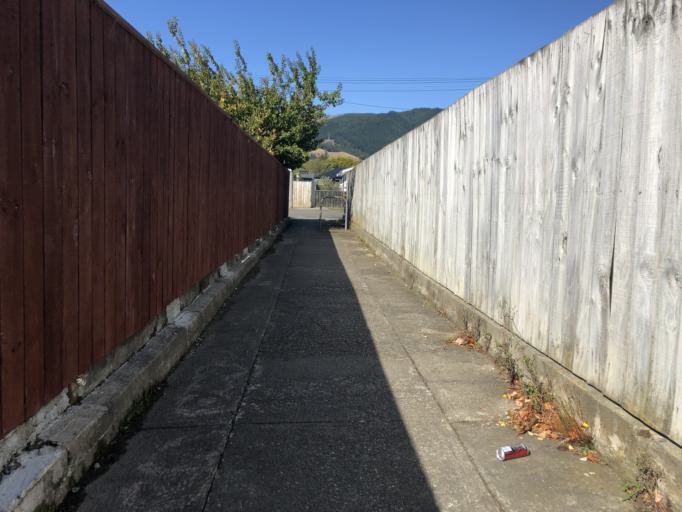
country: NZ
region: Tasman
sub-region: Tasman District
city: Richmond
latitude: -41.3402
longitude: 173.1774
